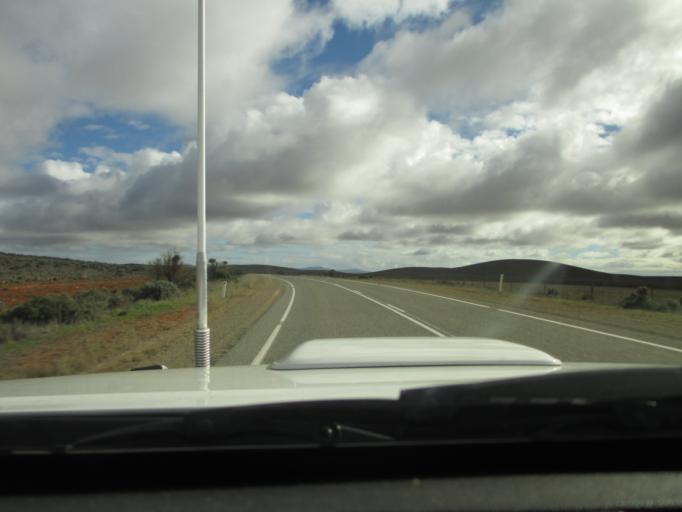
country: AU
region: South Australia
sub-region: Flinders Ranges
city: Quorn
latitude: -32.1595
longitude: 138.5306
